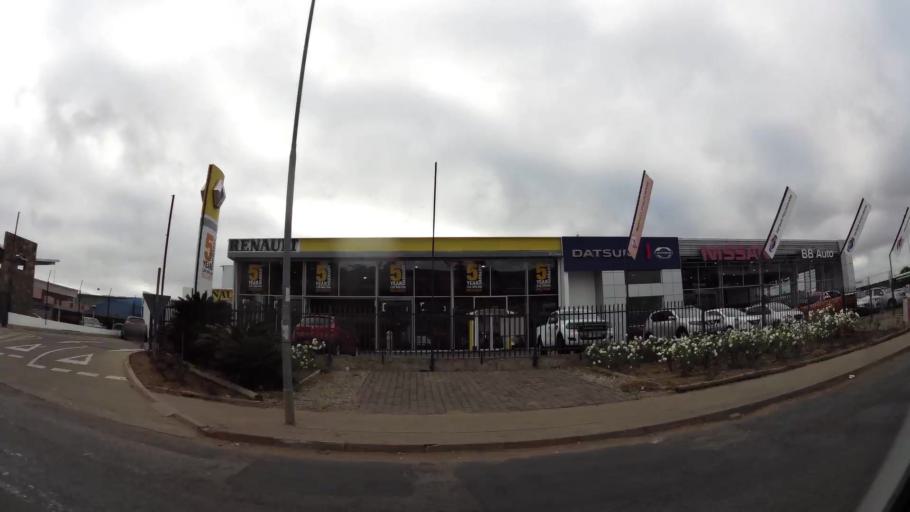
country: ZA
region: Limpopo
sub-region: Capricorn District Municipality
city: Polokwane
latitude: -23.8998
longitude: 29.4505
